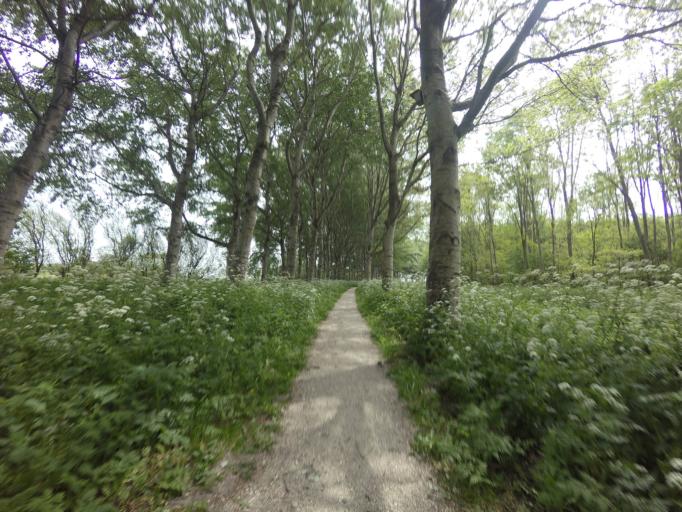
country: NL
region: Friesland
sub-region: Sudwest Fryslan
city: Bolsward
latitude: 53.0974
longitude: 5.4753
